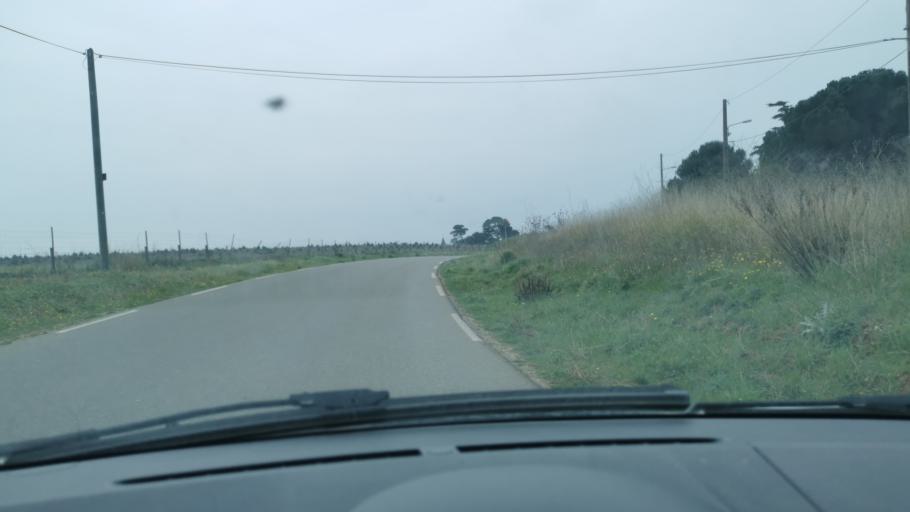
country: FR
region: Languedoc-Roussillon
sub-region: Departement de l'Herault
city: Lattes
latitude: 43.5954
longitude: 3.9153
